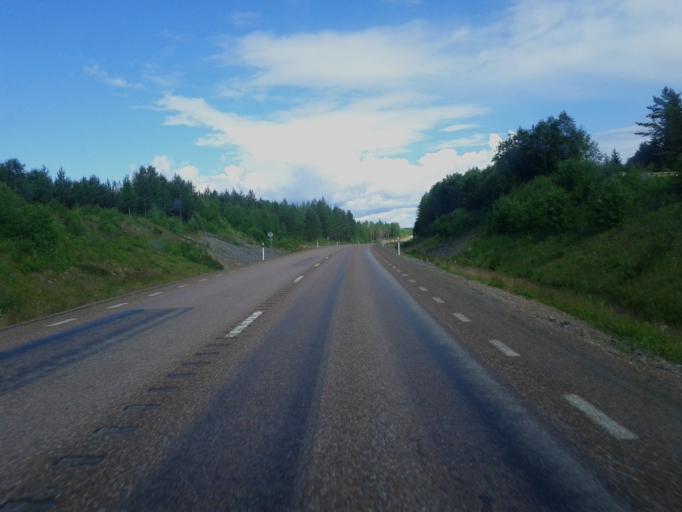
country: SE
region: Dalarna
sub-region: Rattviks Kommun
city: Raettvik
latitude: 60.8458
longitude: 15.1549
